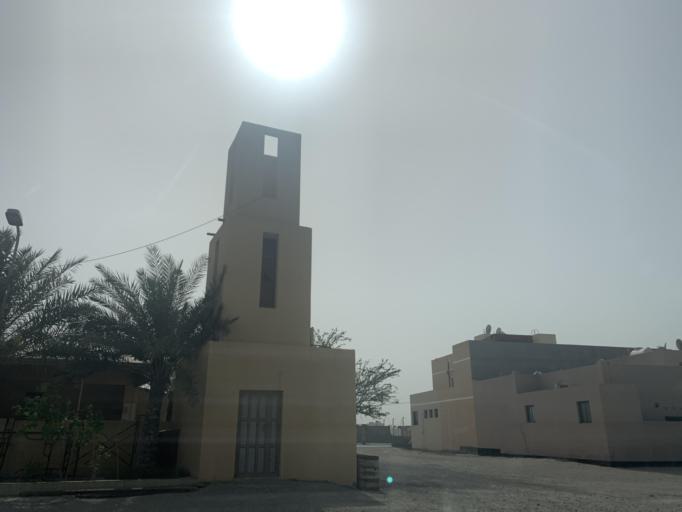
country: BH
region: Northern
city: Sitrah
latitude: 26.1723
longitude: 50.6211
